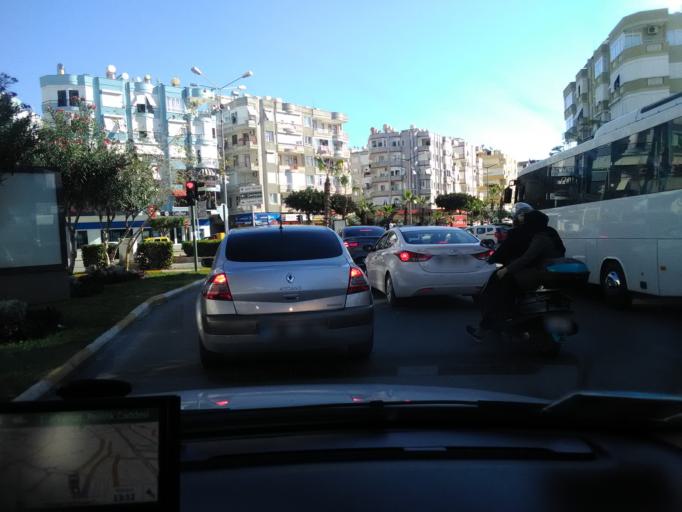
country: TR
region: Antalya
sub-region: Alanya
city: Alanya
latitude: 36.5511
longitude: 31.9881
